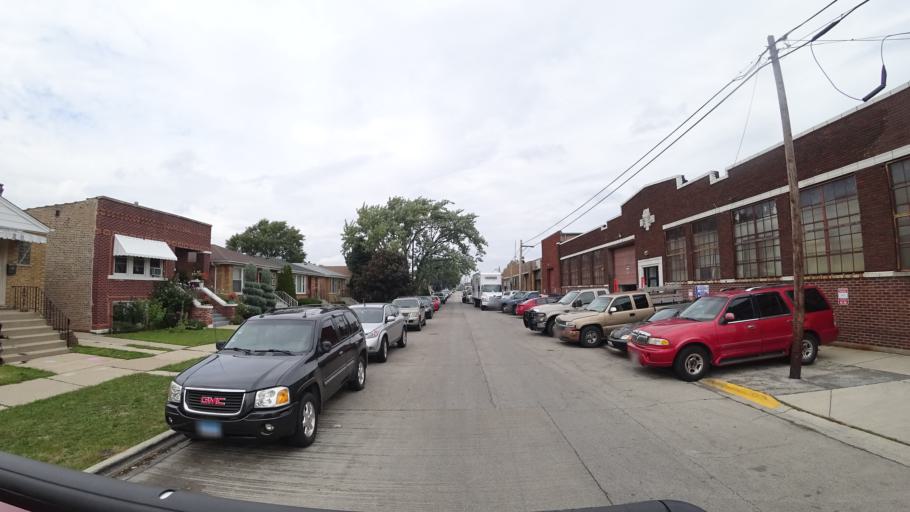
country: US
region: Illinois
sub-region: Cook County
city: Cicero
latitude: 41.8549
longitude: -87.7616
